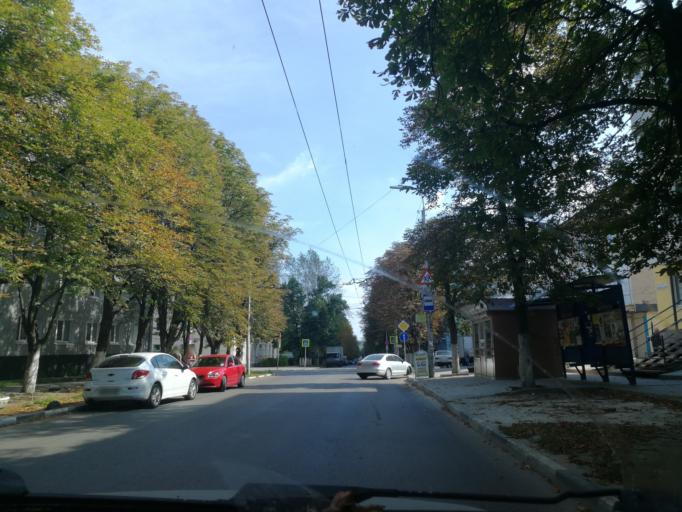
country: RU
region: Rjazan
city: Ryazan'
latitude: 54.6094
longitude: 39.7179
